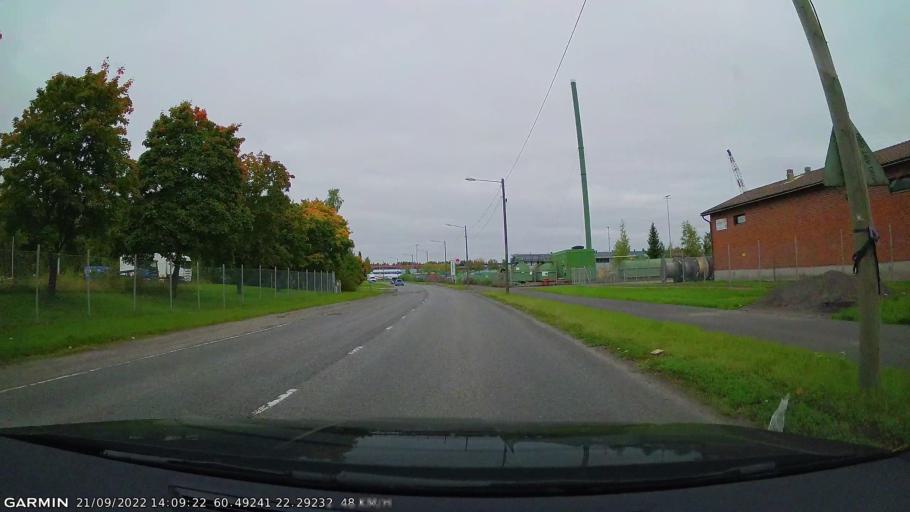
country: FI
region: Varsinais-Suomi
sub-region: Turku
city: Turku
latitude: 60.4927
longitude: 22.2923
